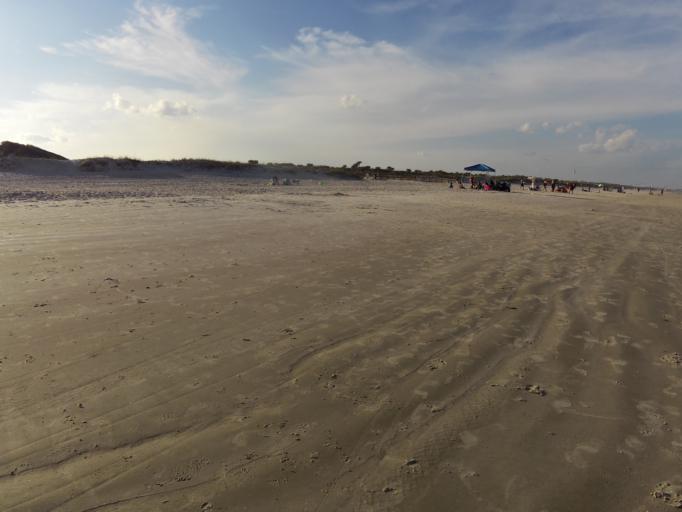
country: US
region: Florida
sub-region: Duval County
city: Atlantic Beach
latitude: 30.3656
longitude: -81.3972
